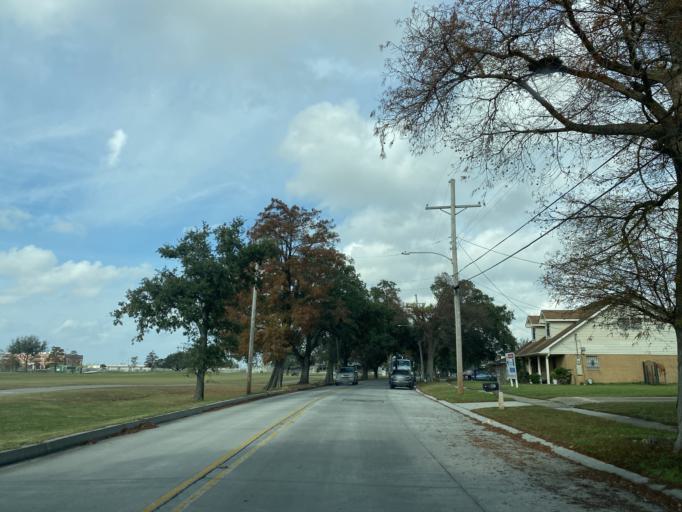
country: US
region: Louisiana
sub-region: Saint Bernard Parish
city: Arabi
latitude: 30.0248
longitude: -90.0386
